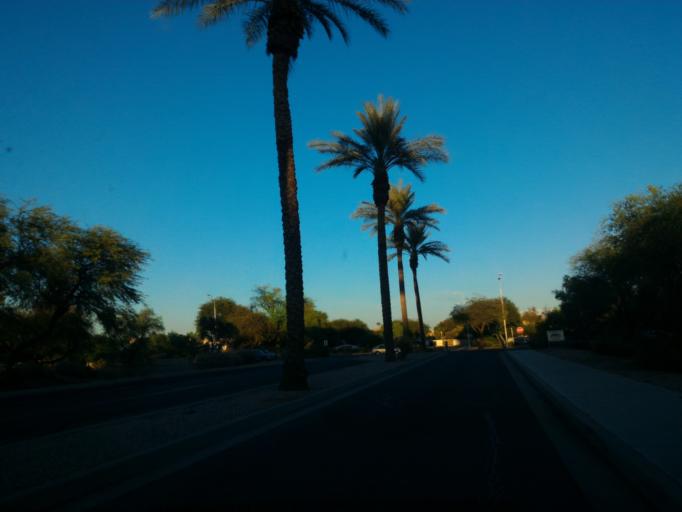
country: US
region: Arizona
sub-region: Maricopa County
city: Guadalupe
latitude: 33.3110
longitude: -111.9294
